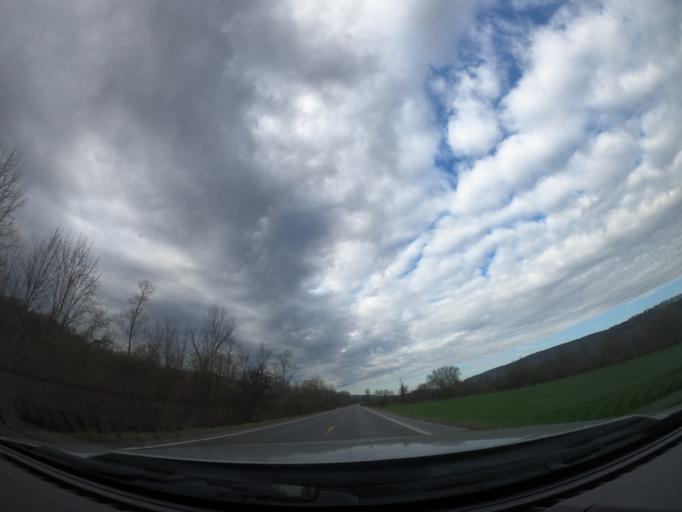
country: US
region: New York
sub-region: Cortland County
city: McGraw
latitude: 42.7309
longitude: -75.9580
